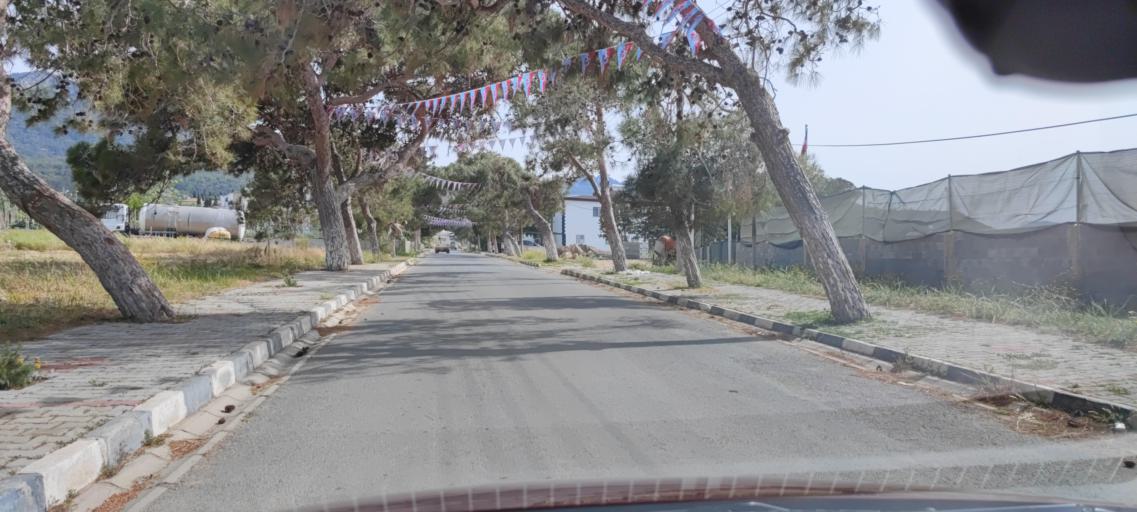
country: CY
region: Ammochostos
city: Trikomo
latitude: 35.4254
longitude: 33.9060
